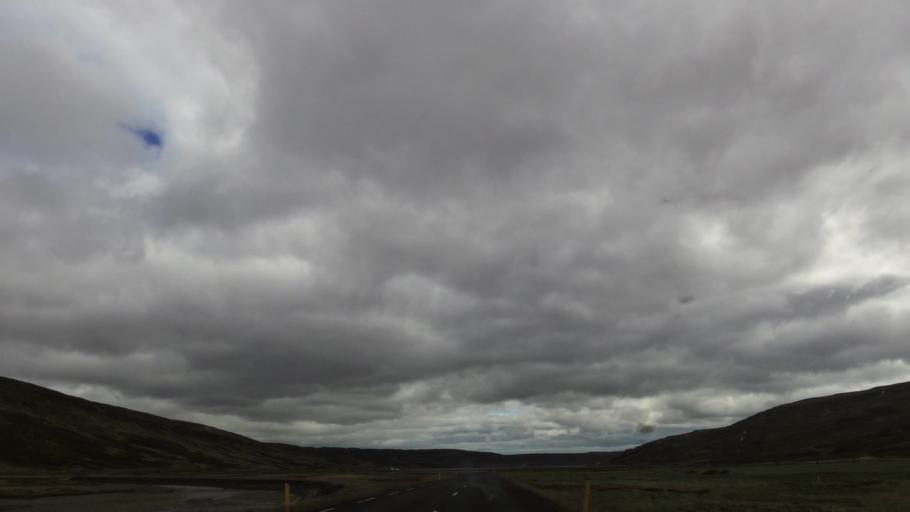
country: IS
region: West
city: Stykkisholmur
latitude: 65.7673
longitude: -21.8219
